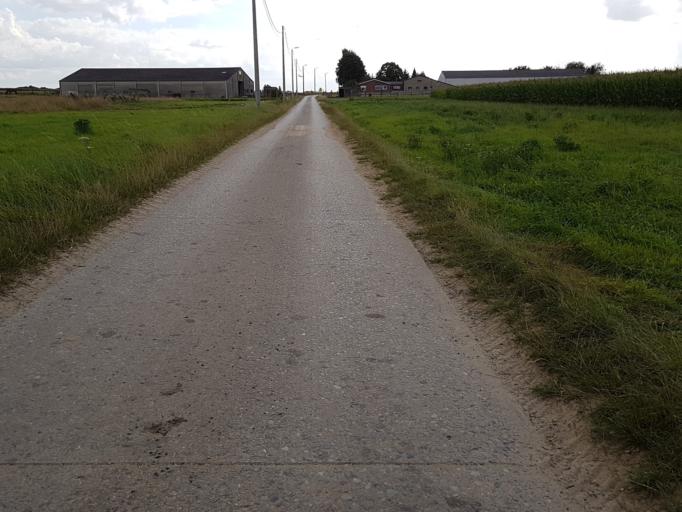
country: BE
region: Flanders
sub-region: Provincie Vlaams-Brabant
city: Kampenhout
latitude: 50.9188
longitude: 4.5580
